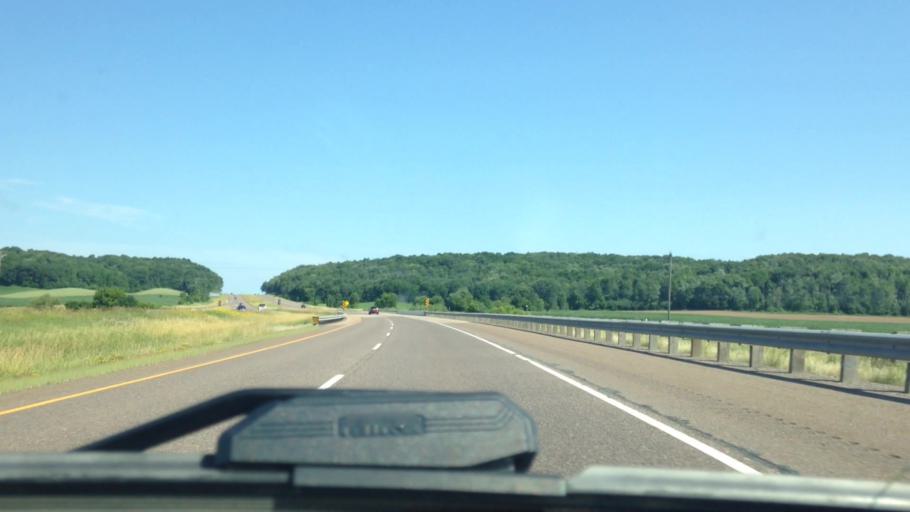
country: US
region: Wisconsin
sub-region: Chippewa County
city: Chippewa Falls
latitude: 44.9645
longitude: -91.4262
